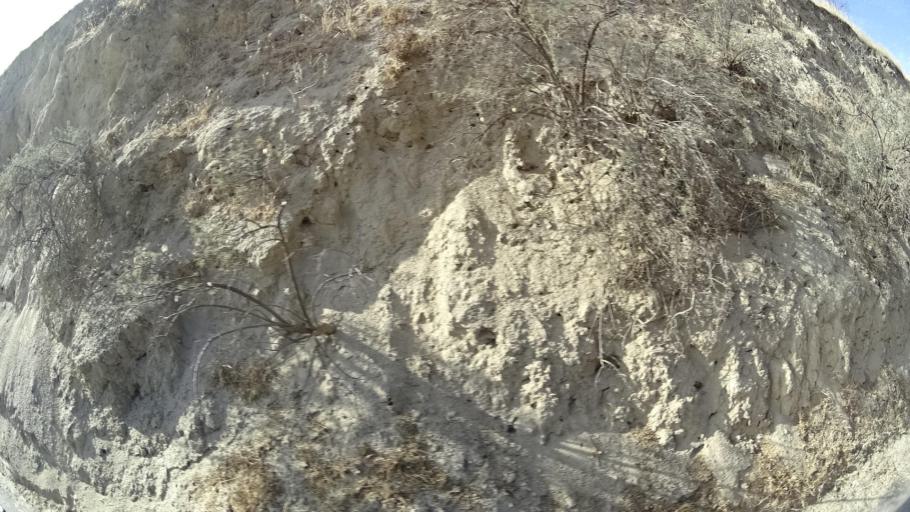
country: US
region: California
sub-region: Kern County
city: Oildale
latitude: 35.5034
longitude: -118.9010
